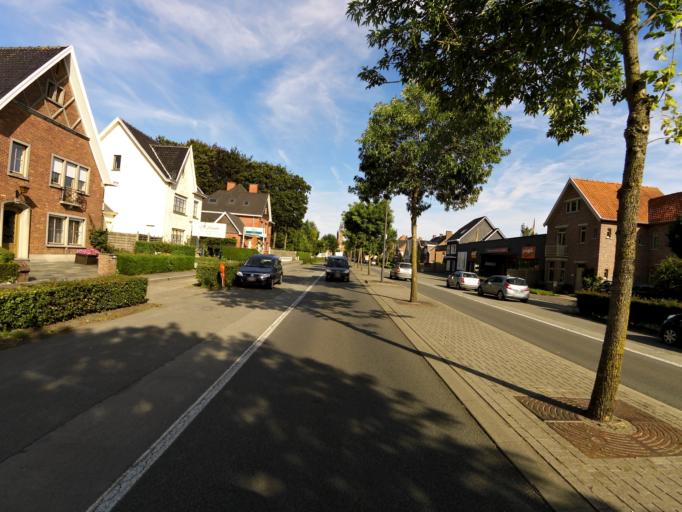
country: BE
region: Flanders
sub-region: Provincie West-Vlaanderen
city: Damme
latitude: 51.2024
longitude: 3.3170
